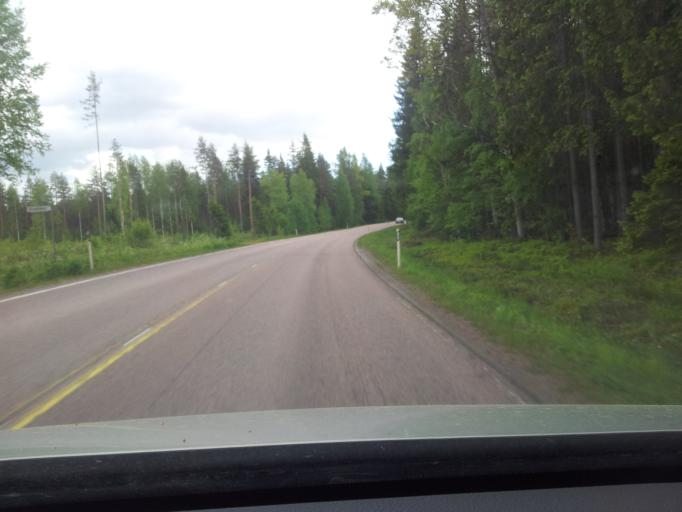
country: FI
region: South Karelia
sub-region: Lappeenranta
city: Luumaeki
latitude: 60.9770
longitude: 27.5506
